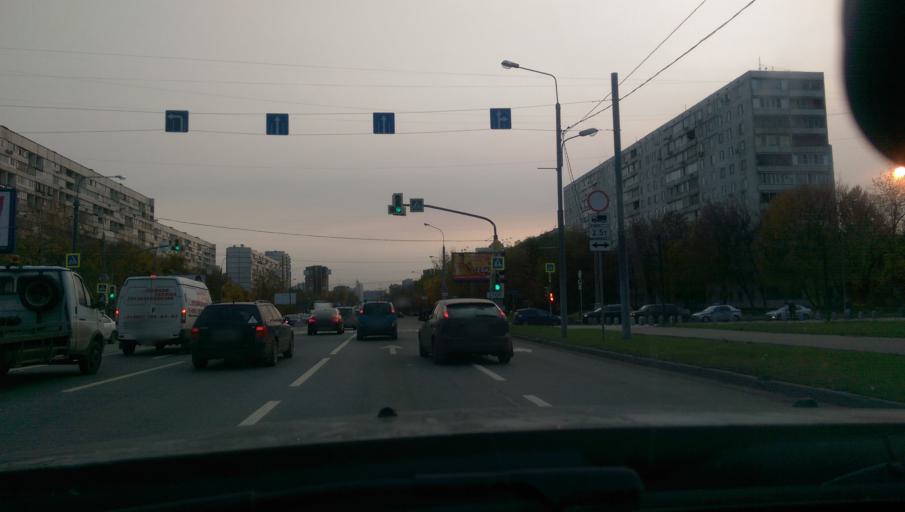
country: RU
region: Moscow
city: Vatutino
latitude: 55.8753
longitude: 37.6672
